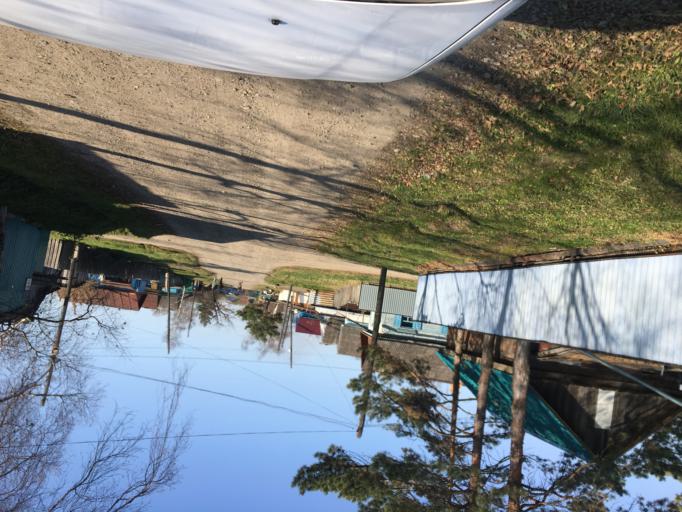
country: RU
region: Primorskiy
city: Dal'nerechensk
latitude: 45.9188
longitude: 133.7140
